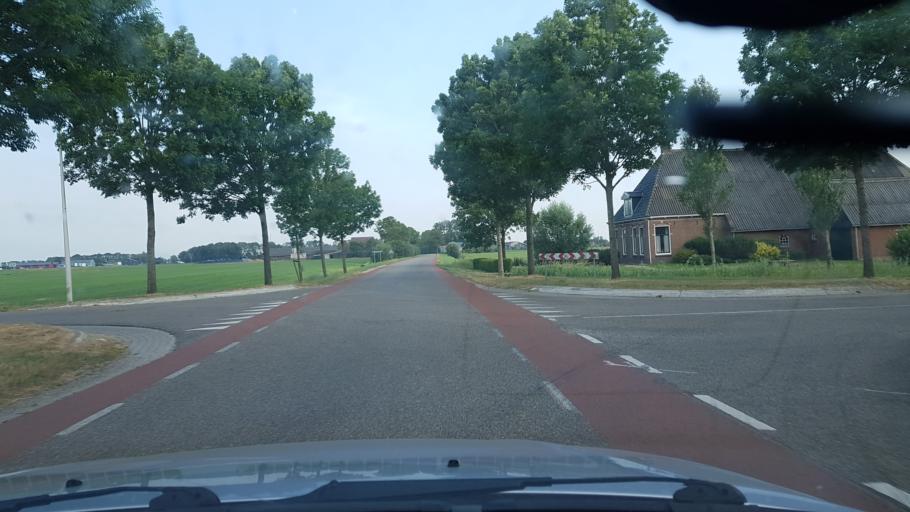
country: NL
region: Friesland
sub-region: Gemeente Ferwerderadiel
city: Burdaard
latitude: 53.3042
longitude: 5.8733
